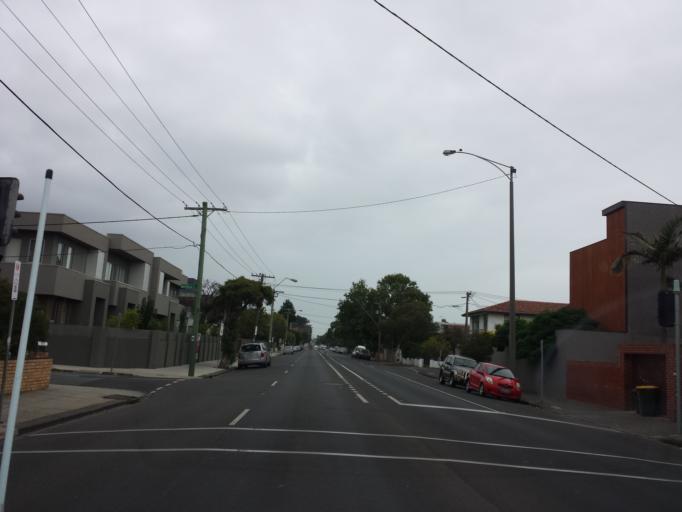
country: AU
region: Victoria
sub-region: Port Phillip
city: Balaclava
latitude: -37.8740
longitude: 144.9986
